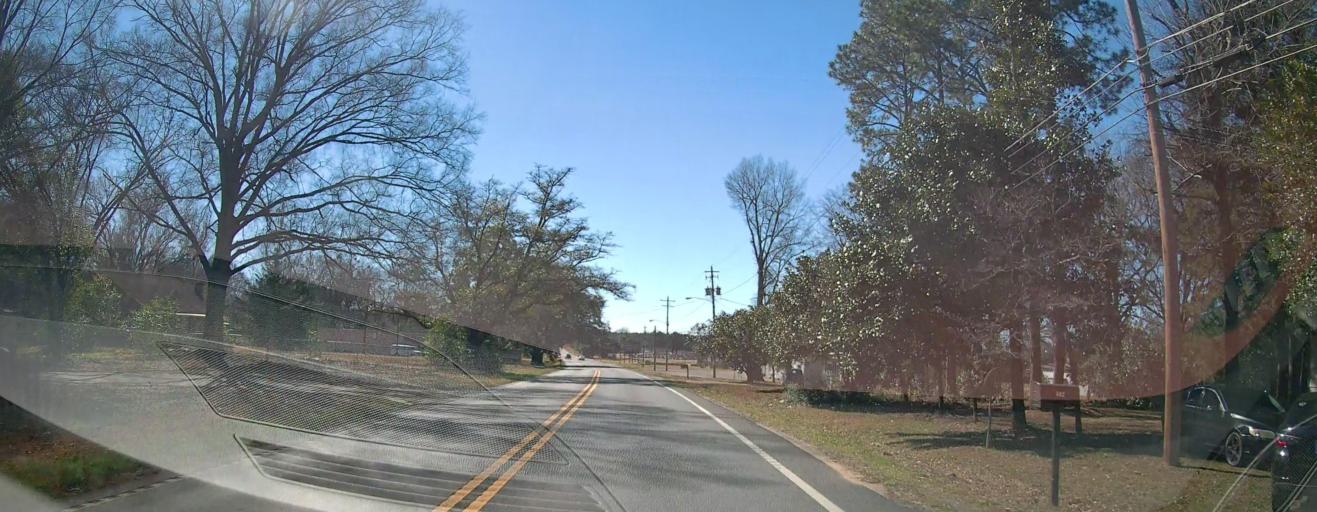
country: US
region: Georgia
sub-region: Peach County
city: Fort Valley
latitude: 32.5477
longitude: -83.8957
